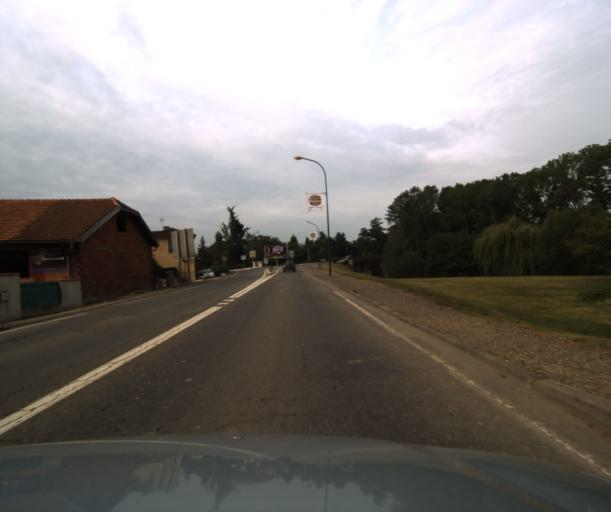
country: FR
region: Midi-Pyrenees
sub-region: Departement du Gers
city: Mirande
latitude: 43.5165
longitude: 0.4130
